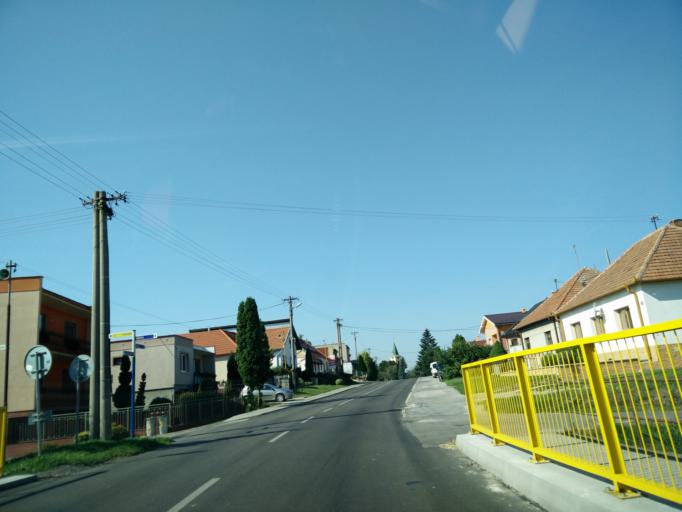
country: SK
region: Nitriansky
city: Banovce nad Bebravou
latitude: 48.5401
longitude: 18.2063
